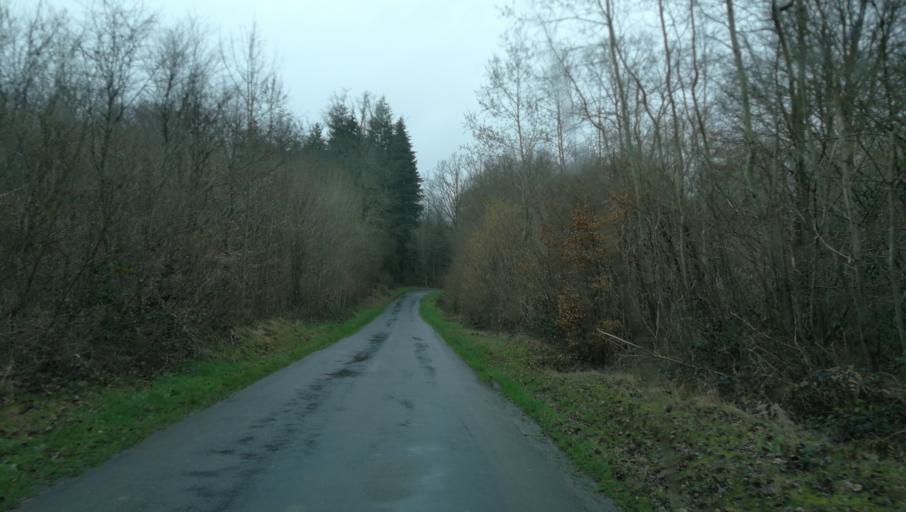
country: FR
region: Haute-Normandie
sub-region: Departement de l'Eure
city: Brionne
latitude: 49.1826
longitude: 0.6971
